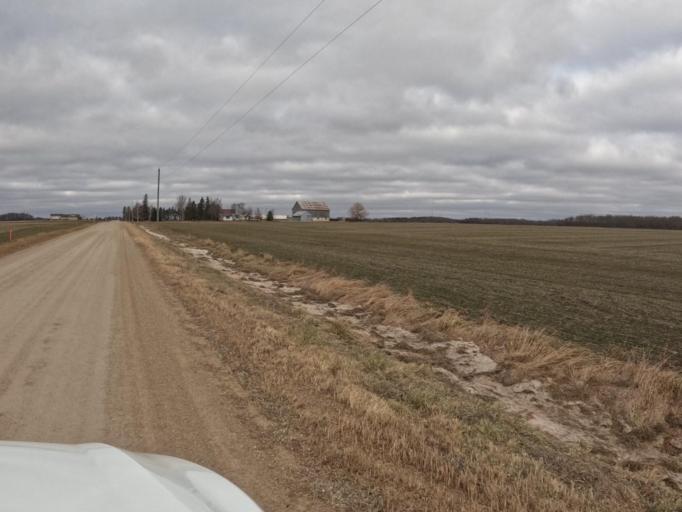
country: CA
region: Ontario
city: Shelburne
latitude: 43.8578
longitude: -80.3991
